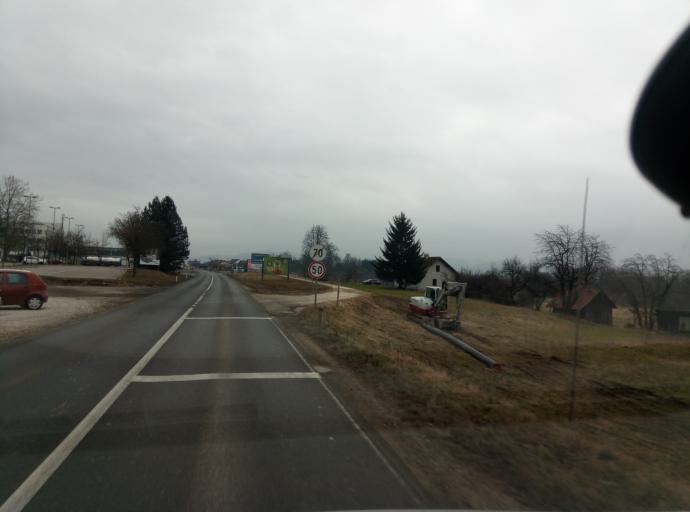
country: SI
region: Dol pri Ljubljani
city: Dol pri Ljubljani
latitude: 46.0915
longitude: 14.5730
